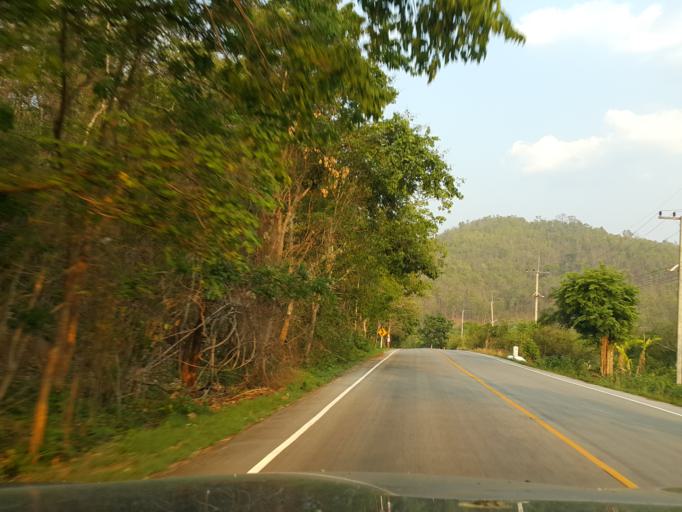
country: TH
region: Lamphun
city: Li
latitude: 17.8424
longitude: 99.0080
